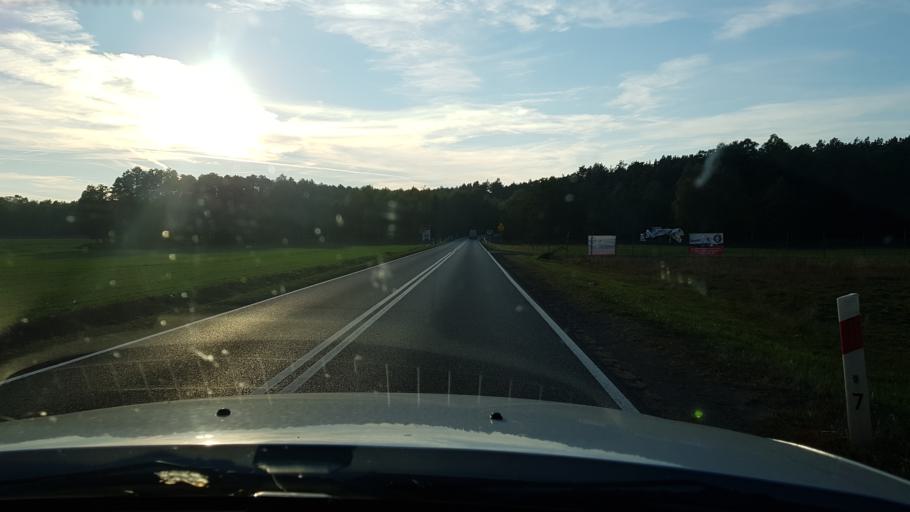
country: PL
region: West Pomeranian Voivodeship
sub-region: Powiat gryfinski
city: Chojna
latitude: 52.9662
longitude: 14.3958
